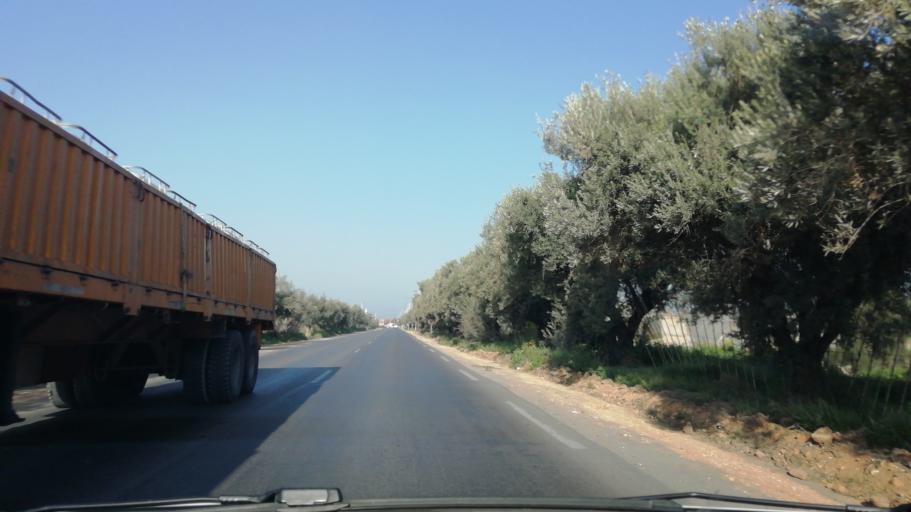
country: DZ
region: Mostaganem
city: Mostaganem
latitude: 35.7504
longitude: 0.1259
